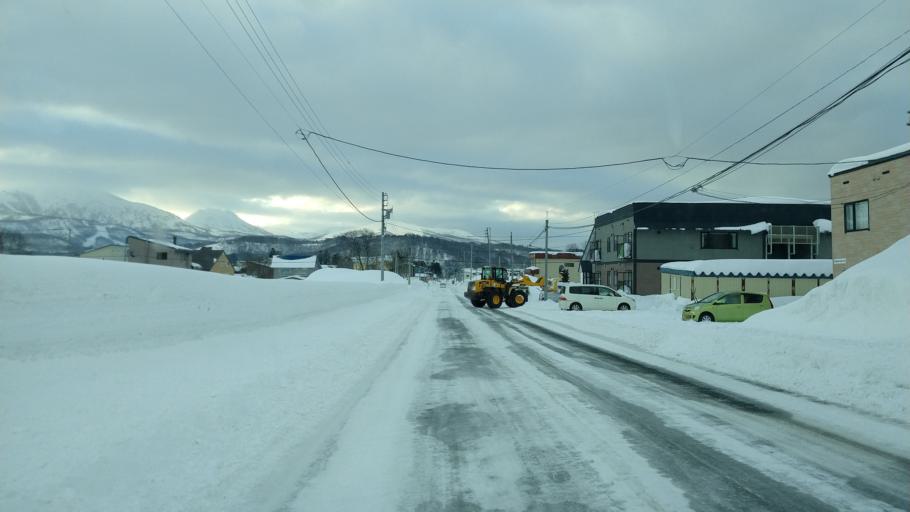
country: JP
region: Hokkaido
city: Niseko Town
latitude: 42.9086
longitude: 140.7615
